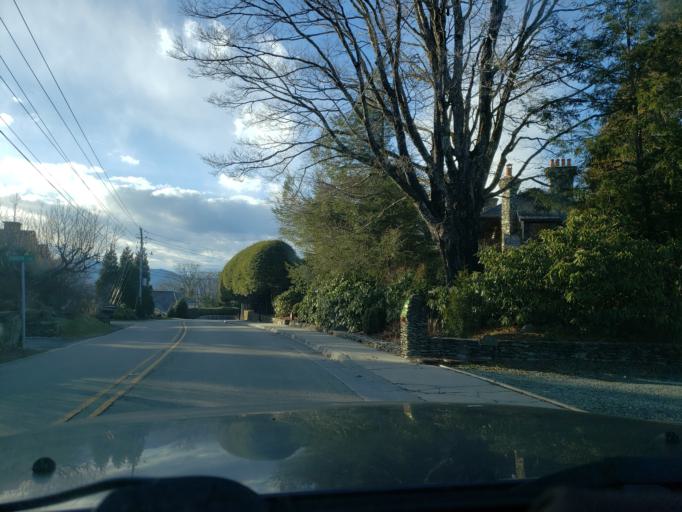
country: US
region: North Carolina
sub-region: Watauga County
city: Blowing Rock
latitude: 36.1243
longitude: -81.6767
